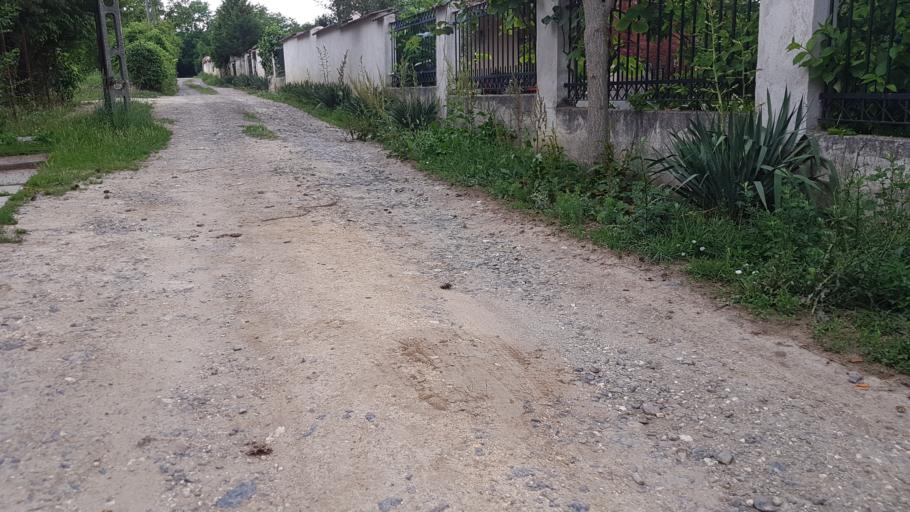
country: HU
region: Pest
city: Budakalasz
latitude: 47.6127
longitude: 19.0467
